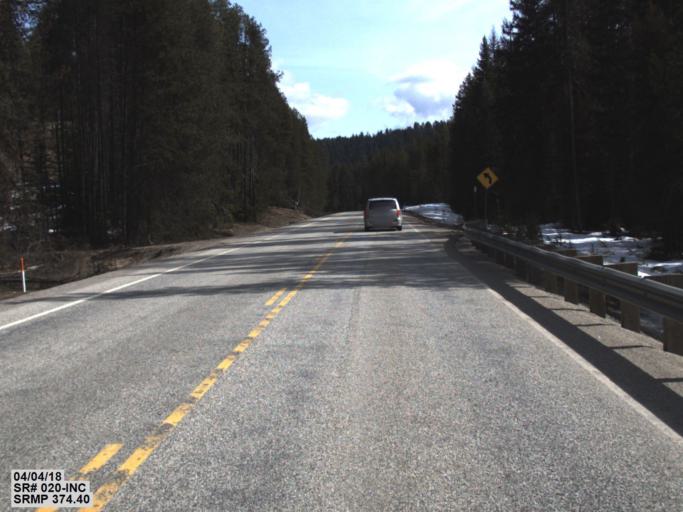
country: US
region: Washington
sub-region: Stevens County
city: Chewelah
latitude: 48.5496
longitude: -117.5688
